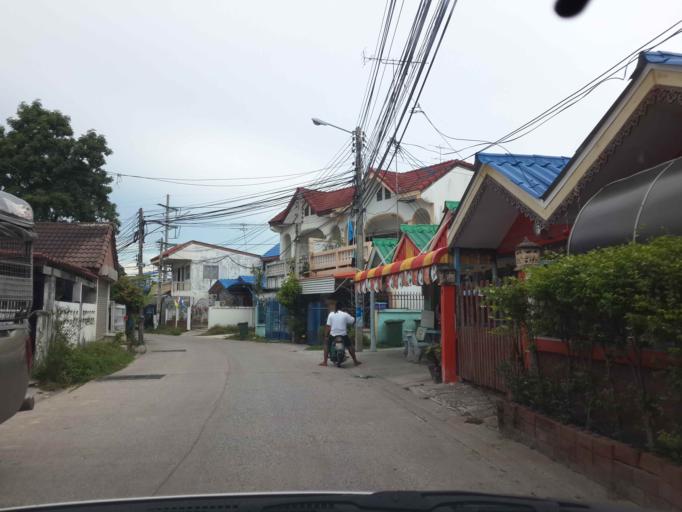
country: TH
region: Chon Buri
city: Si Racha
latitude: 13.2216
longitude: 100.9411
